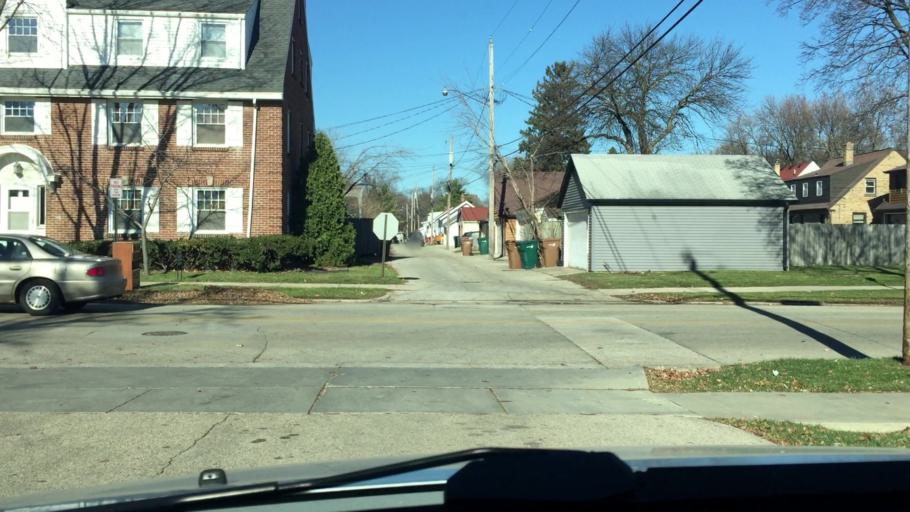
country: US
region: Wisconsin
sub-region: Milwaukee County
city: Whitefish Bay
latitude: 43.1000
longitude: -87.9201
